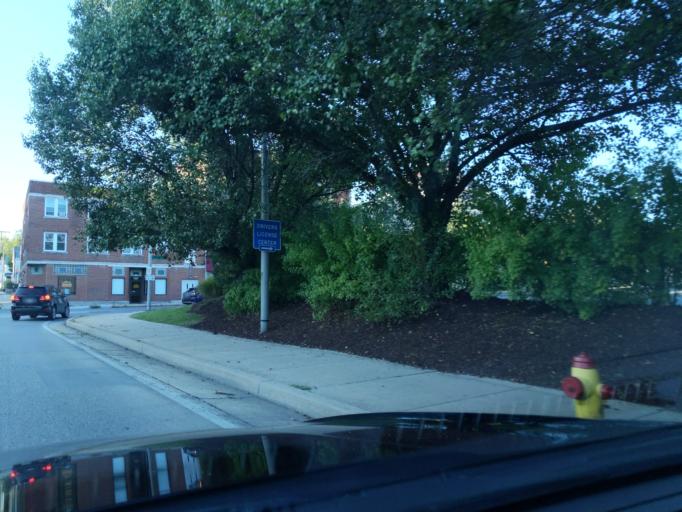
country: US
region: Pennsylvania
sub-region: Blair County
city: Altoona
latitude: 40.5122
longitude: -78.4081
